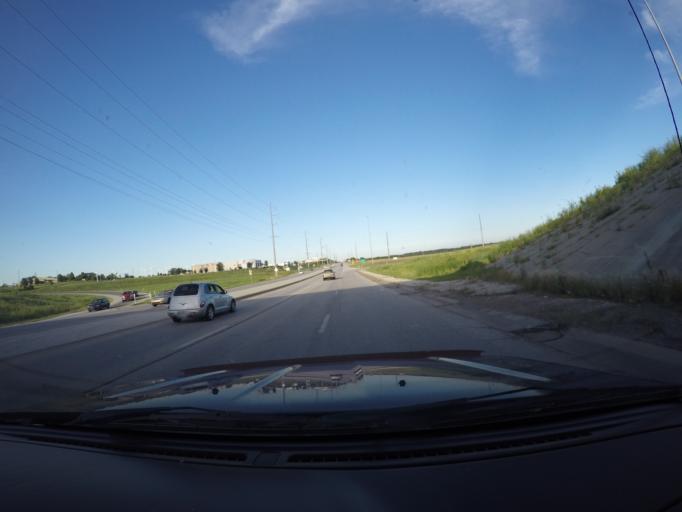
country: US
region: Kansas
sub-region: Wyandotte County
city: Edwardsville
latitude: 39.1285
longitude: -94.8161
